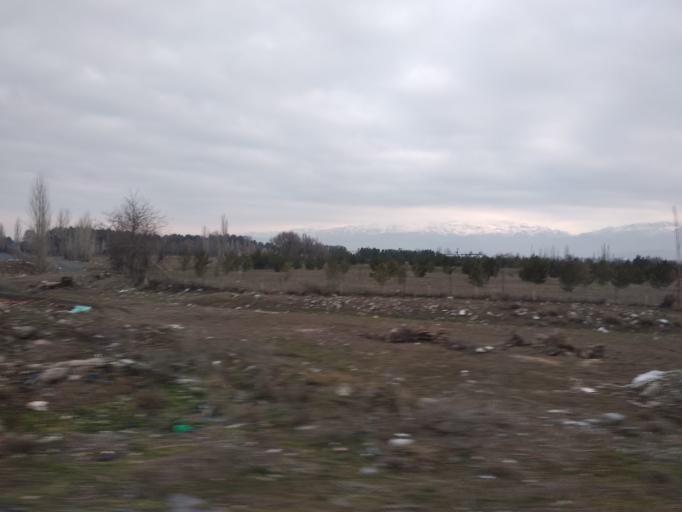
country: TR
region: Erzincan
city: Erzincan
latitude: 39.7195
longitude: 39.4840
